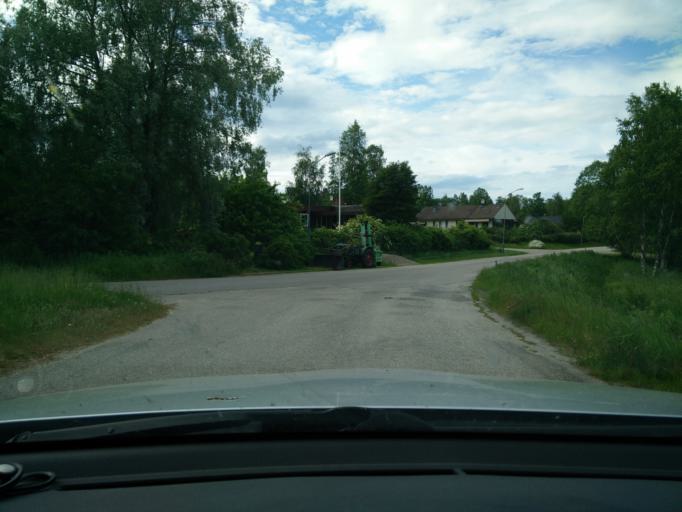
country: SE
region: Gaevleborg
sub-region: Nordanstigs Kommun
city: Bergsjoe
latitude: 61.9770
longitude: 17.0526
